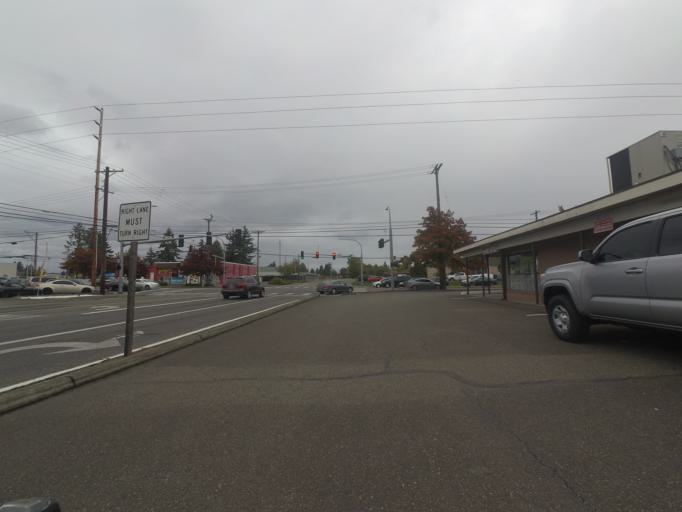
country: US
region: Washington
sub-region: Pierce County
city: Lakewood
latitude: 47.1557
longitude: -122.5051
